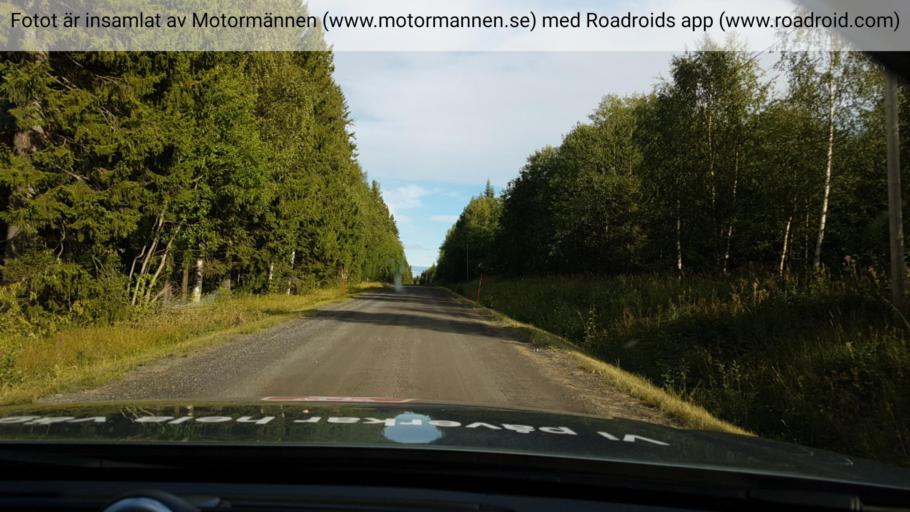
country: SE
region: Jaemtland
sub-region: Stroemsunds Kommun
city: Stroemsund
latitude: 64.1408
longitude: 15.7378
